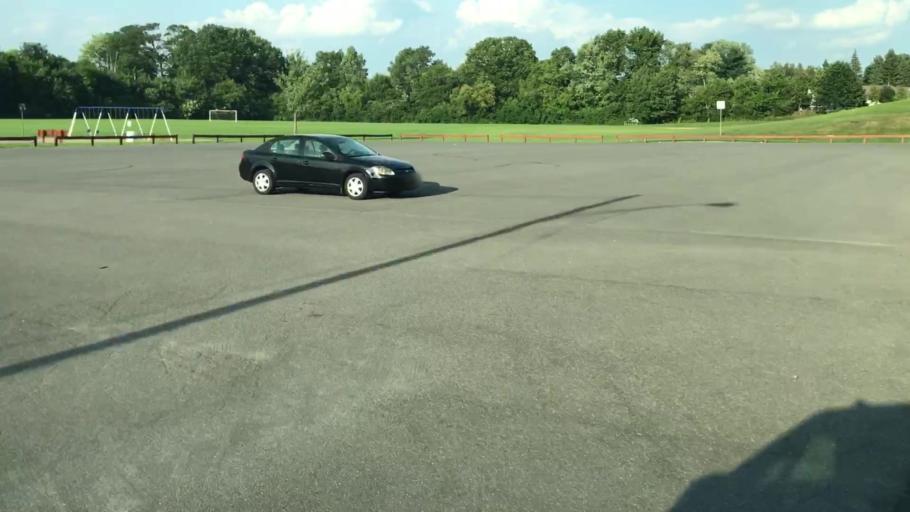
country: US
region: New York
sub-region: Onondaga County
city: Mattydale
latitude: 43.1196
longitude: -76.1568
